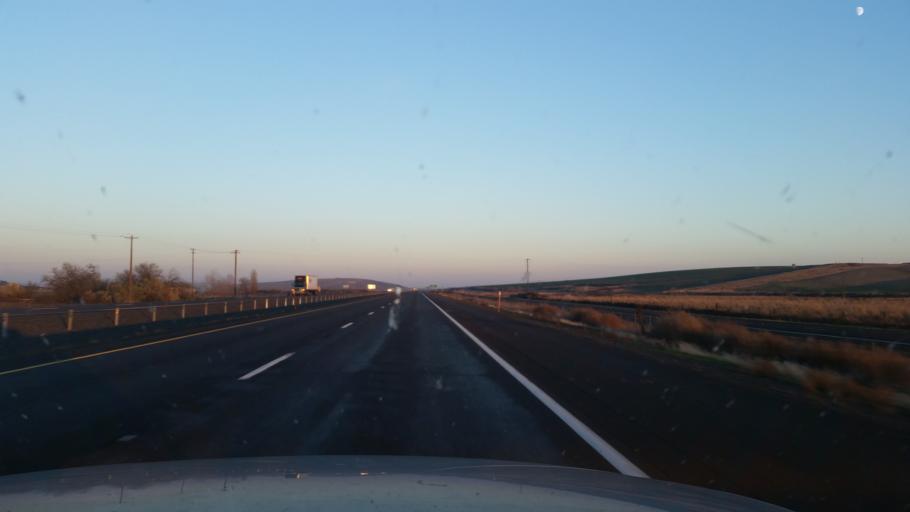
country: US
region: Washington
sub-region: Grant County
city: Warden
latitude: 47.0852
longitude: -119.0243
